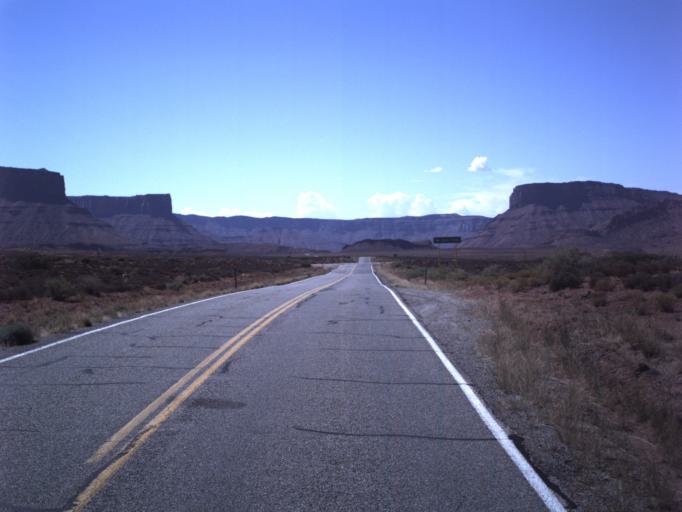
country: US
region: Utah
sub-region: Grand County
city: Moab
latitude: 38.7253
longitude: -109.3536
